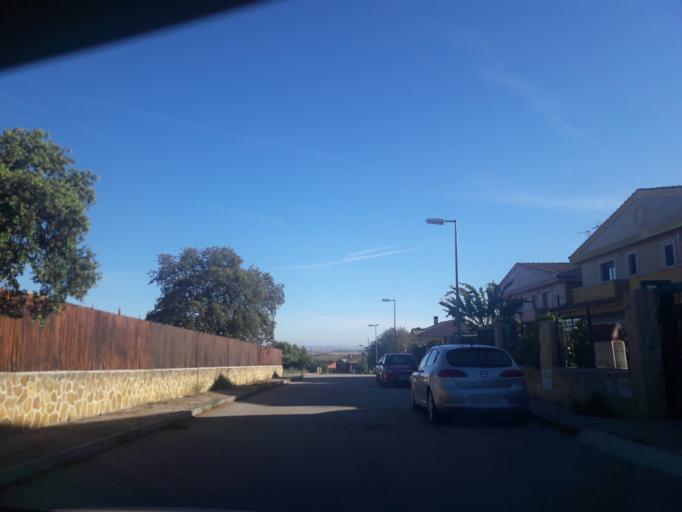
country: ES
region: Castille and Leon
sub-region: Provincia de Salamanca
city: Martinamor
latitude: 40.8093
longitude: -5.6410
